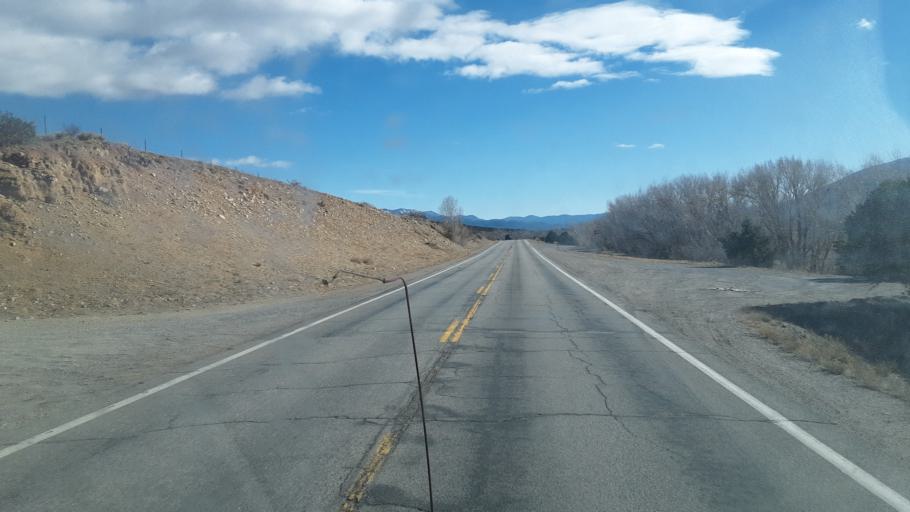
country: US
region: Colorado
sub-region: Chaffee County
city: Salida
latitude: 38.5362
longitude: -106.1712
